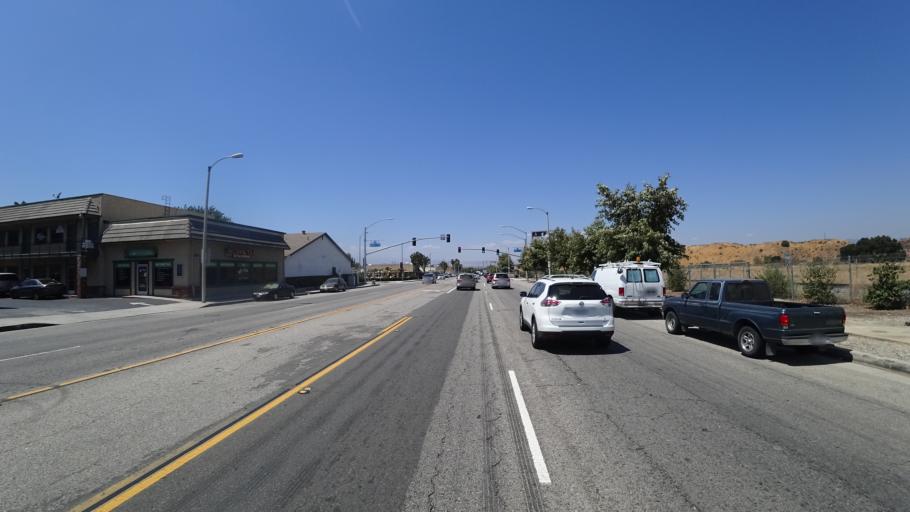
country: US
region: California
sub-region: Los Angeles County
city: Santa Clarita
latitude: 34.3877
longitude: -118.5335
